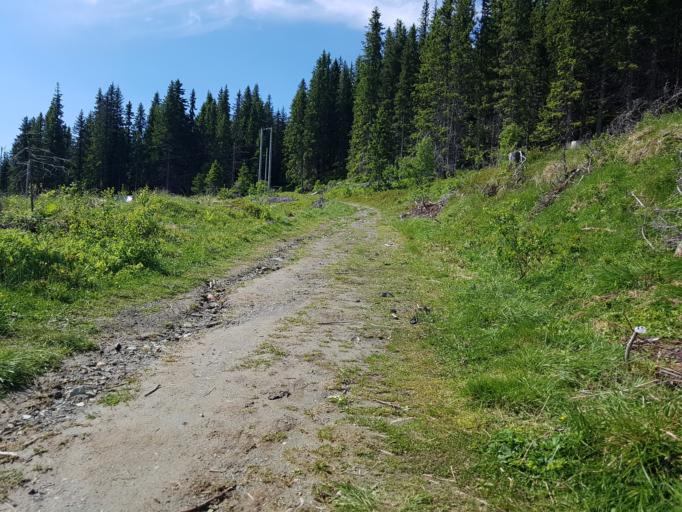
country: NO
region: Sor-Trondelag
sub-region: Trondheim
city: Trondheim
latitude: 63.4163
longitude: 10.2727
